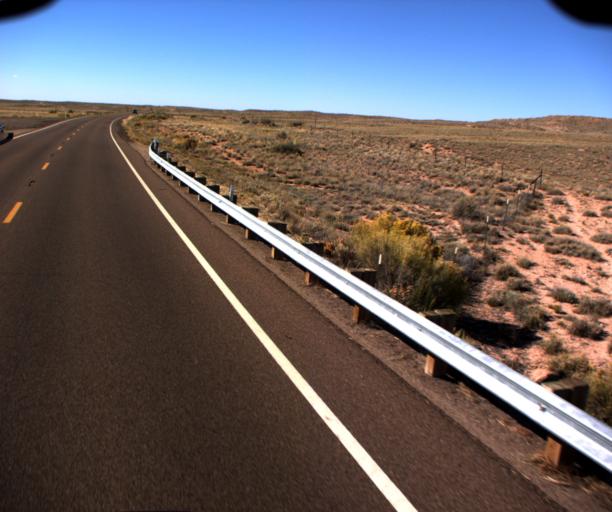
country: US
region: Arizona
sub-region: Navajo County
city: Joseph City
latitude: 35.1707
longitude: -110.4463
